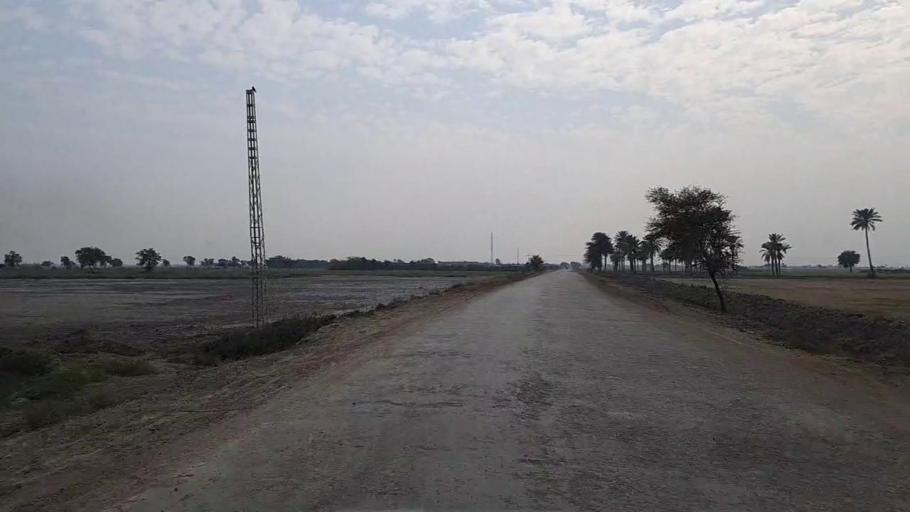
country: PK
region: Sindh
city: Mirwah Gorchani
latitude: 25.3893
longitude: 69.0818
